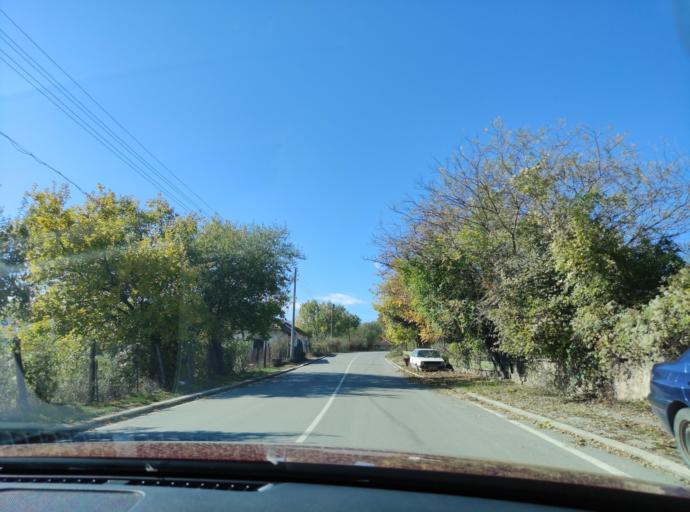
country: BG
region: Montana
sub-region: Obshtina Chiprovtsi
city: Chiprovtsi
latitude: 43.4329
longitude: 22.9803
